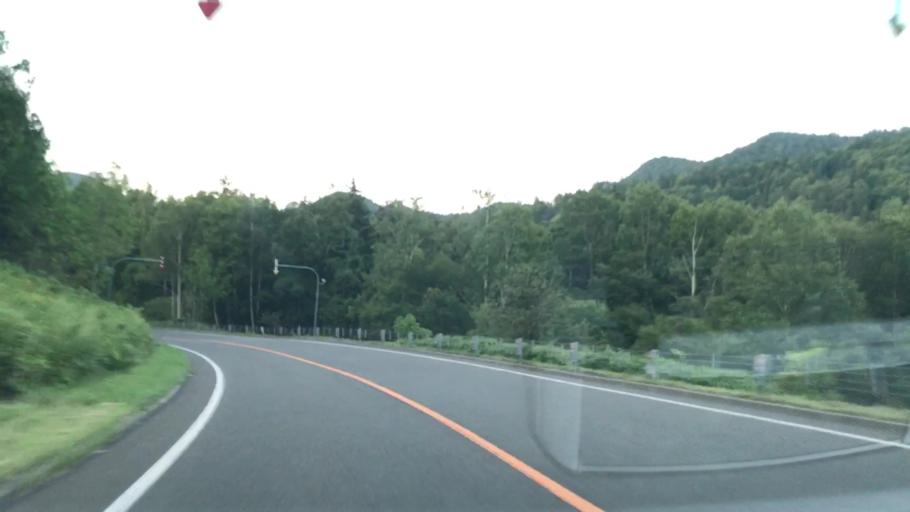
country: JP
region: Hokkaido
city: Sapporo
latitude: 42.9048
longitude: 141.1212
